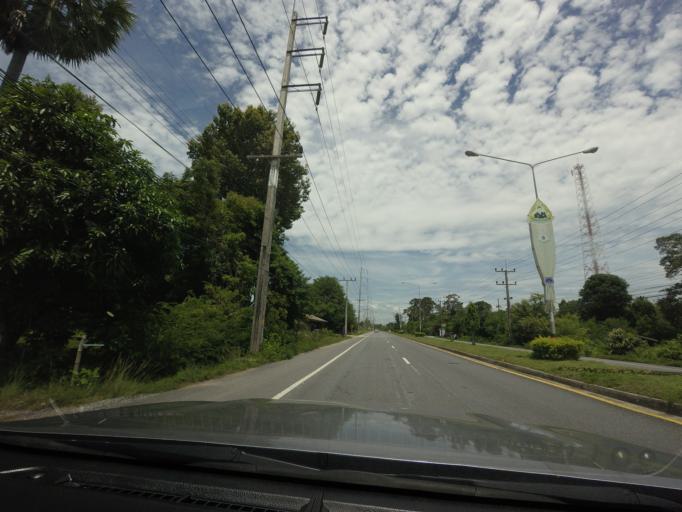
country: TH
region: Songkhla
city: Sathing Phra
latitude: 7.5576
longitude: 100.4138
